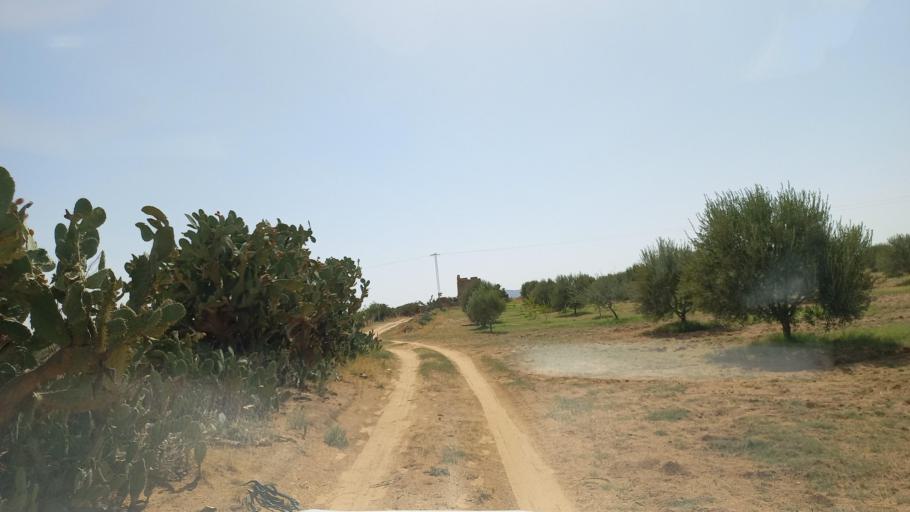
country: TN
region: Al Qasrayn
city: Kasserine
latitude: 35.2267
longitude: 9.0365
